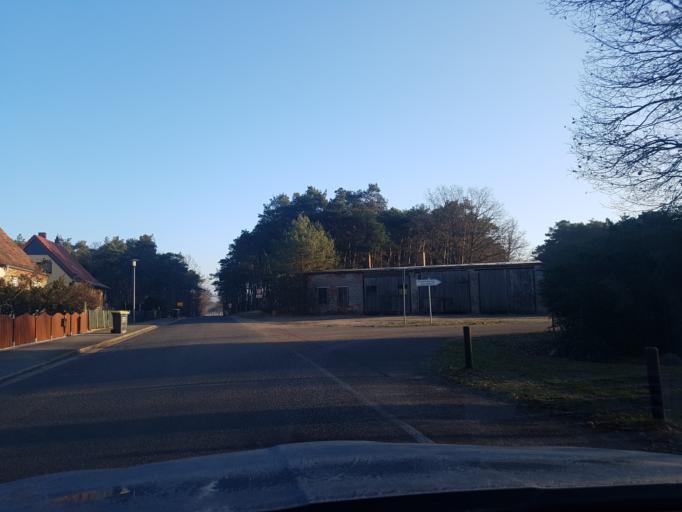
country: DE
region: Brandenburg
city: Schlieben
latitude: 51.6970
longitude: 13.3313
